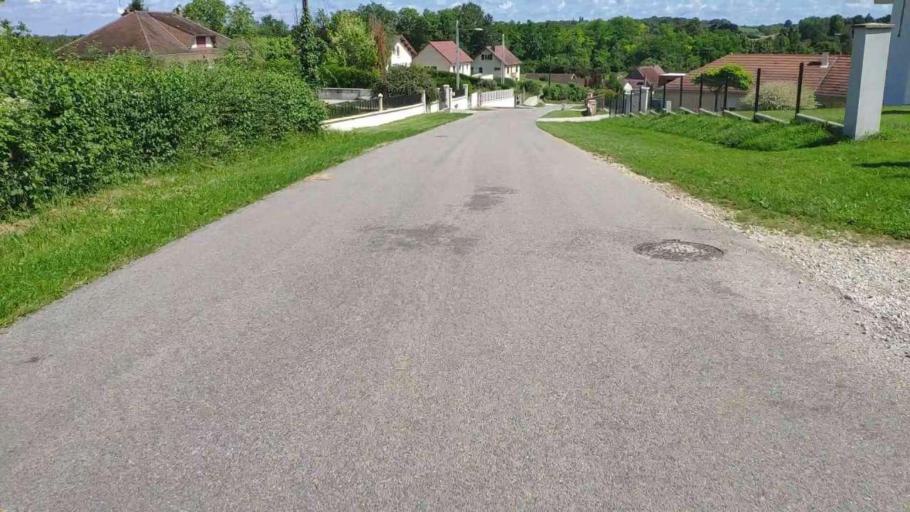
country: FR
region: Franche-Comte
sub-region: Departement du Jura
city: Bletterans
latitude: 46.8240
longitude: 5.5591
